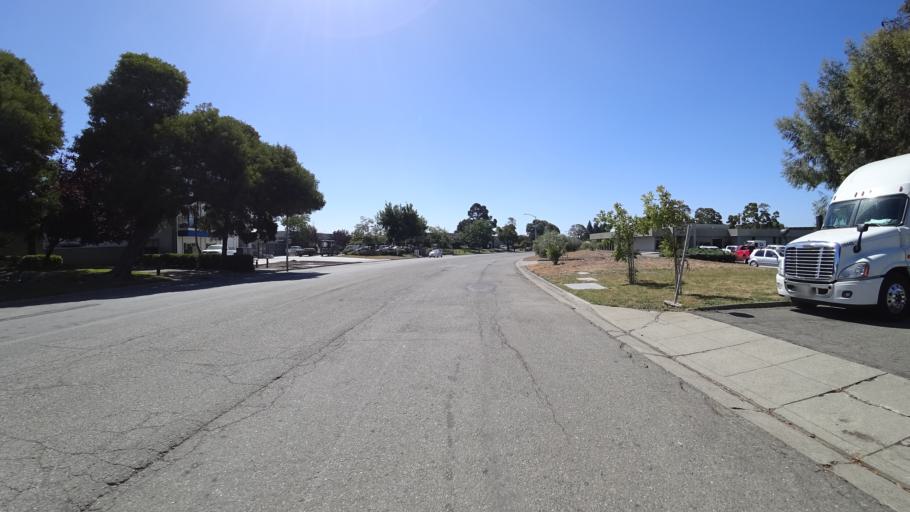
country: US
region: California
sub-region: Alameda County
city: San Lorenzo
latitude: 37.6574
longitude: -122.1259
